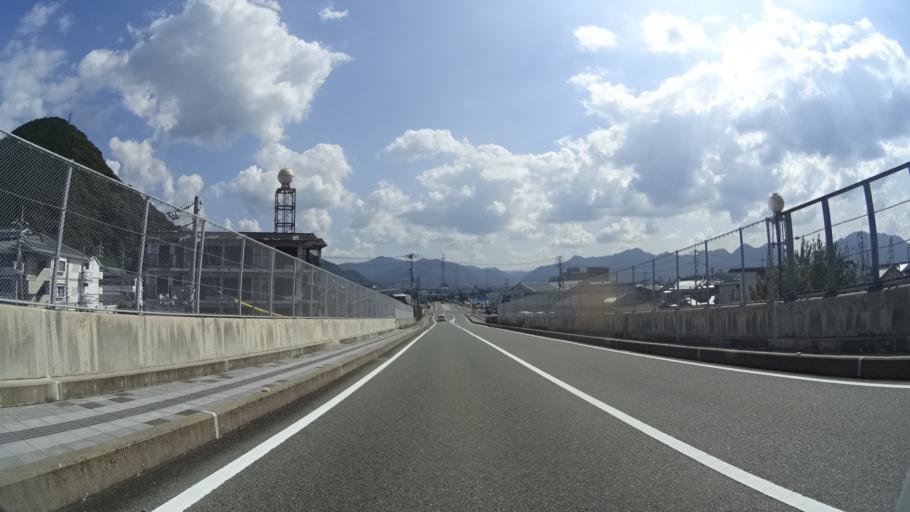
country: JP
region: Yamaguchi
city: Hagi
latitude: 34.4230
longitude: 131.4126
